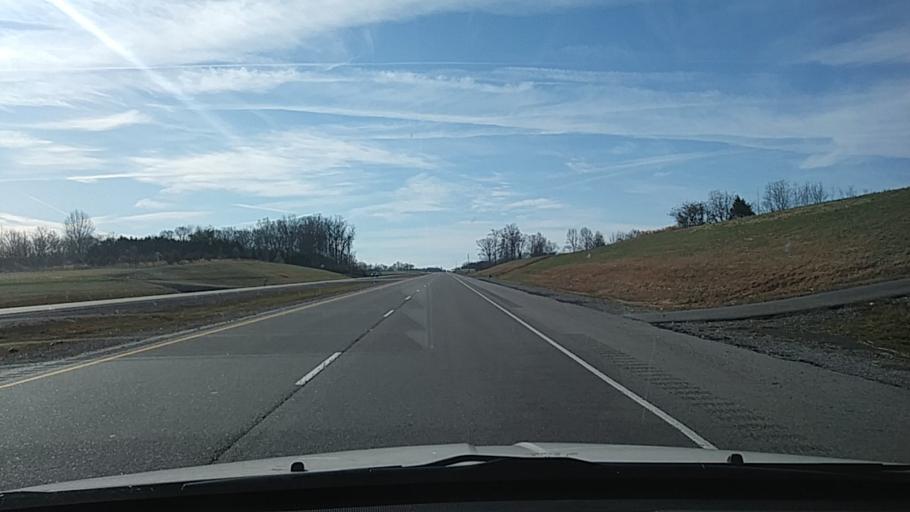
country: US
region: Tennessee
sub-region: Sumner County
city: Portland
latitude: 36.5213
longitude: -86.5097
